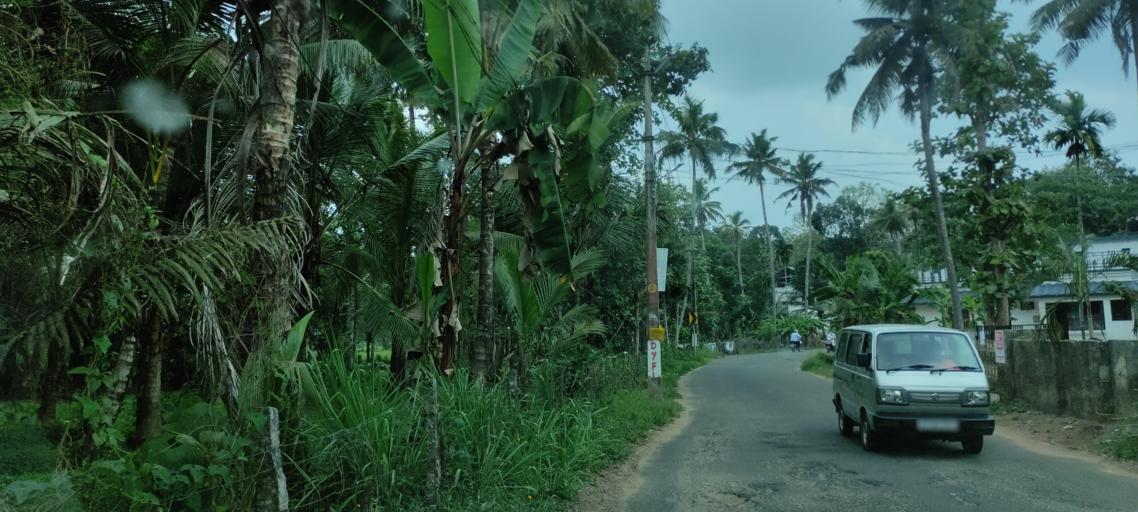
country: IN
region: Kerala
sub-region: Pattanamtitta
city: Adur
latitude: 9.1615
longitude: 76.7339
